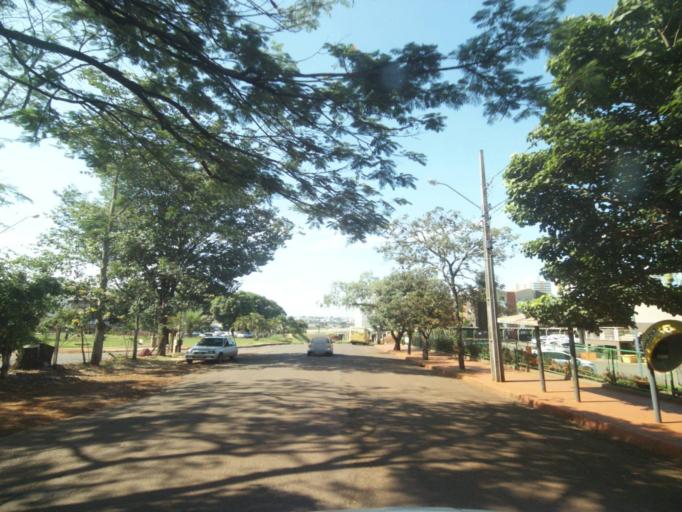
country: BR
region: Parana
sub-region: Londrina
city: Londrina
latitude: -23.3258
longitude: -51.1939
